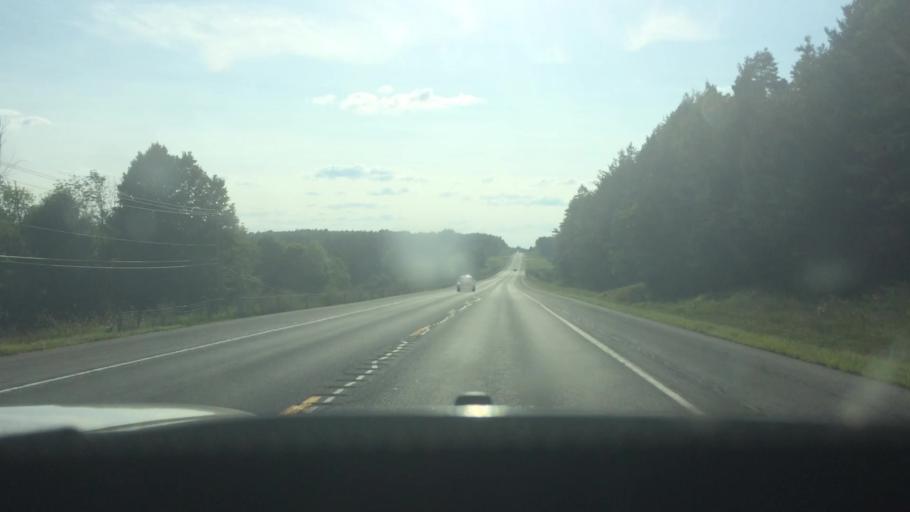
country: US
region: New York
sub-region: St. Lawrence County
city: Potsdam
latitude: 44.6729
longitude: -74.8608
